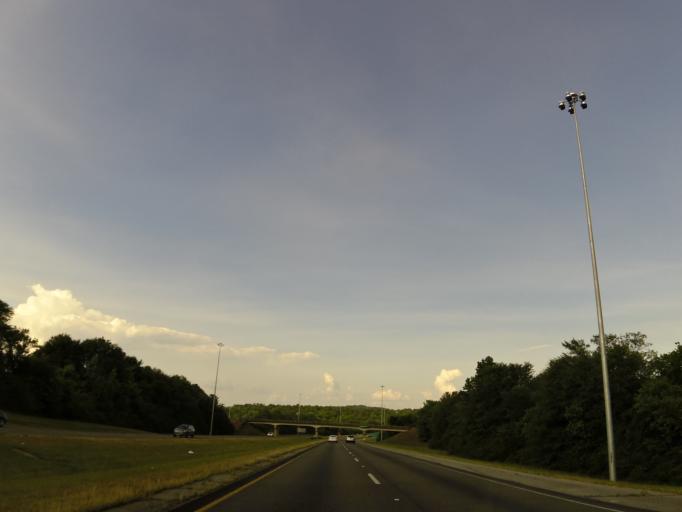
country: US
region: Alabama
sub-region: Jefferson County
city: Trussville
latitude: 33.6558
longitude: -86.5974
